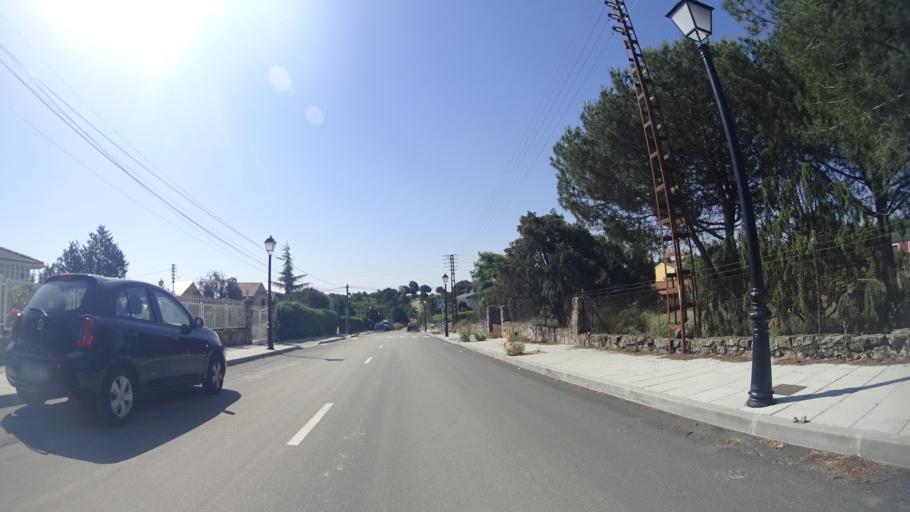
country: ES
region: Madrid
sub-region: Provincia de Madrid
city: Hoyo de Manzanares
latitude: 40.6013
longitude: -3.9097
